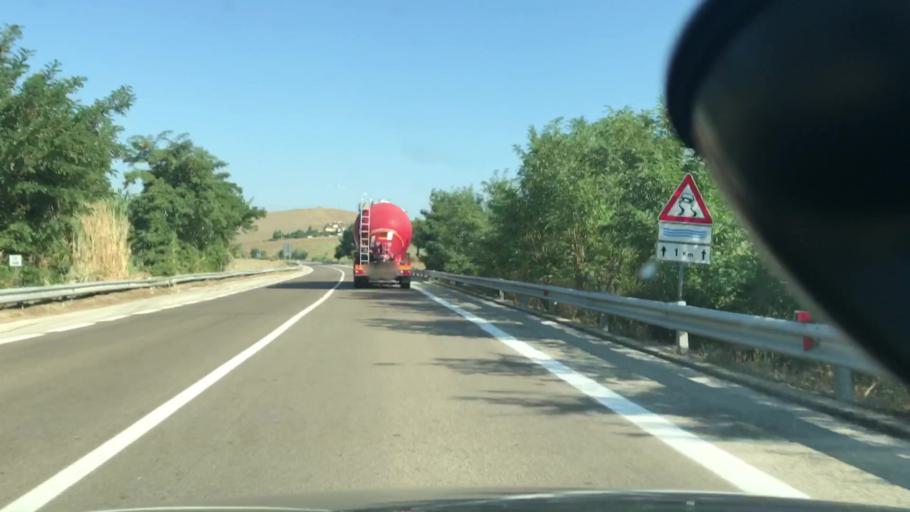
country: IT
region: Basilicate
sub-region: Provincia di Matera
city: Irsina
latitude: 40.8050
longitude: 16.2735
